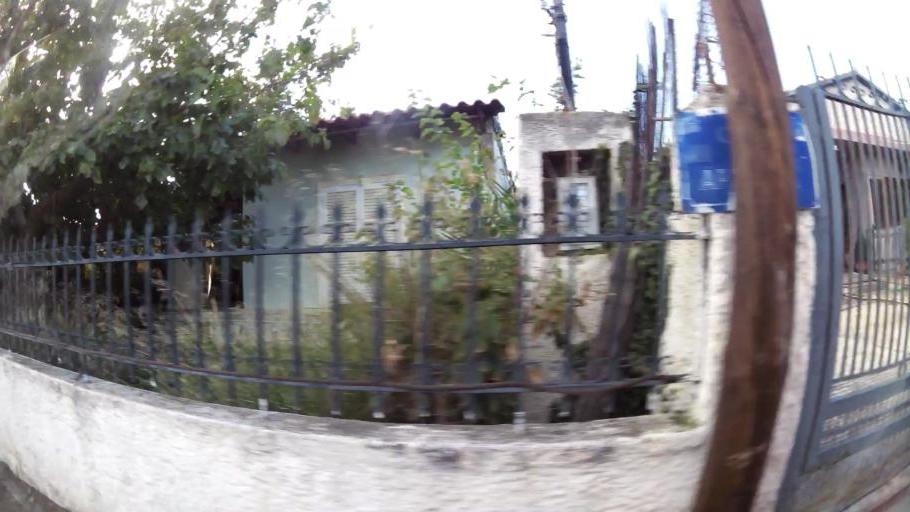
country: GR
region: Attica
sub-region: Nomarchia Anatolikis Attikis
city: Thrakomakedones
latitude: 38.1206
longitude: 23.7320
